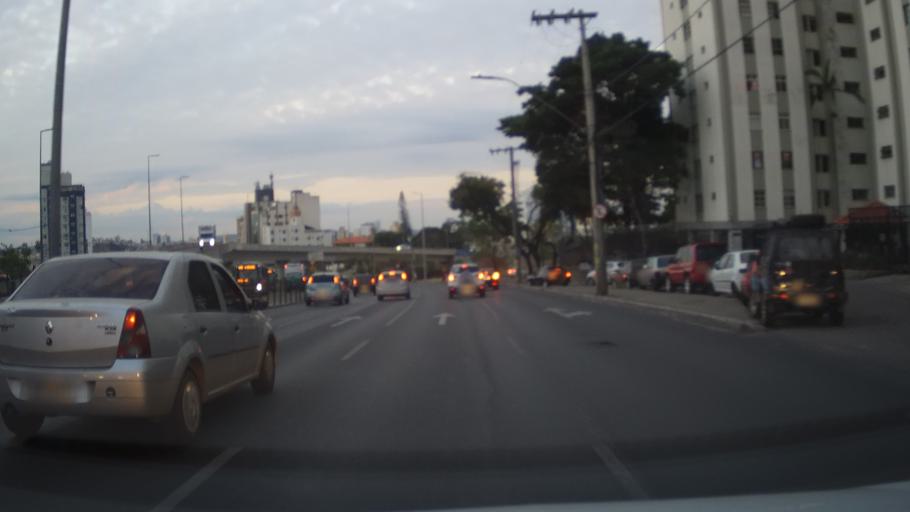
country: BR
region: Minas Gerais
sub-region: Belo Horizonte
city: Belo Horizonte
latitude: -19.8964
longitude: -43.9273
